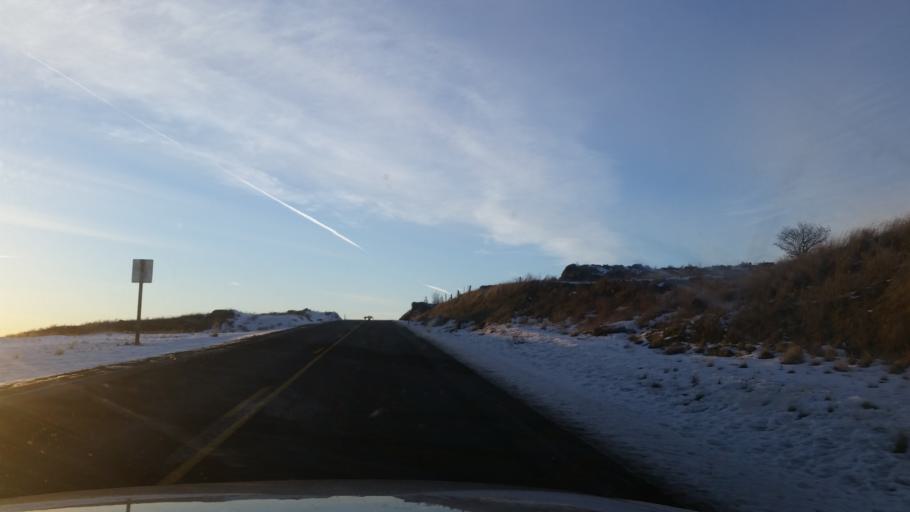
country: US
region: Washington
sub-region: Spokane County
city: Cheney
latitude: 47.1169
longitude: -117.7371
